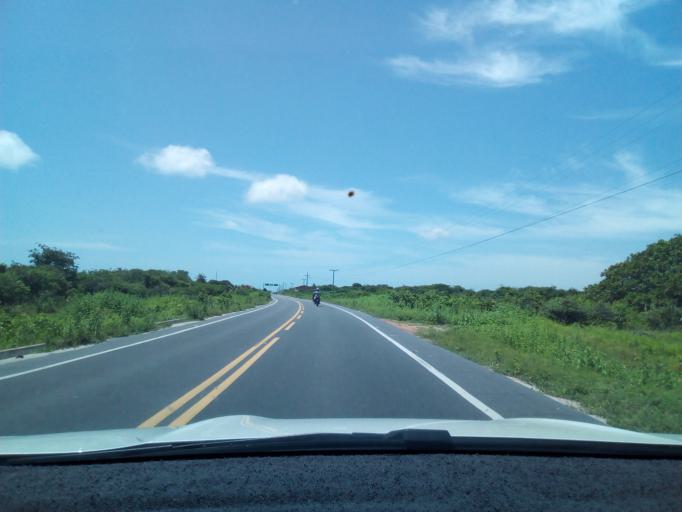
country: BR
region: Ceara
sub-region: Aracati
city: Aracati
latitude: -4.3941
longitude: -37.8672
